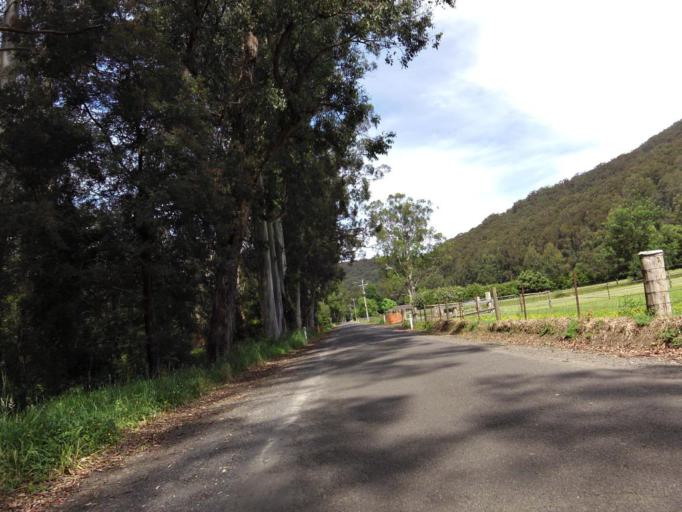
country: AU
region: Victoria
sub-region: Yarra Ranges
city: Millgrove
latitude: -37.7500
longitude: 145.7183
